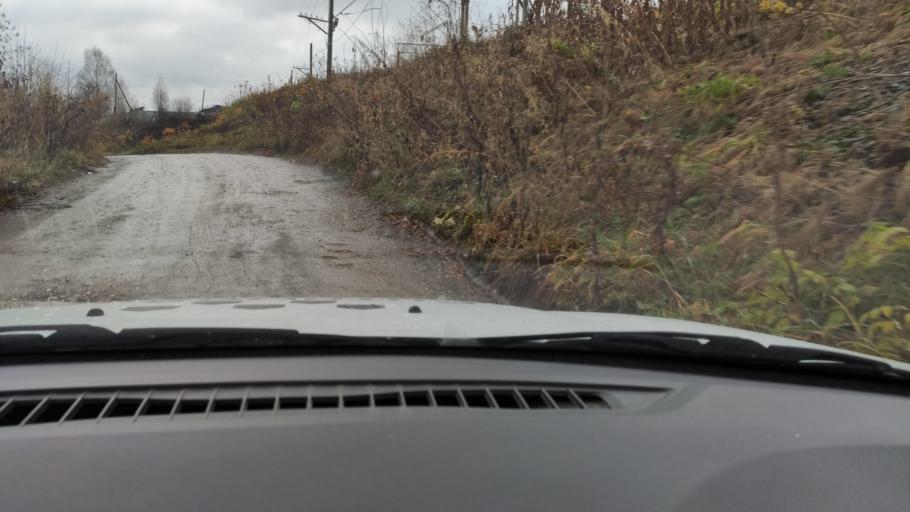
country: RU
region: Perm
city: Sylva
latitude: 58.0448
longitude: 56.7401
